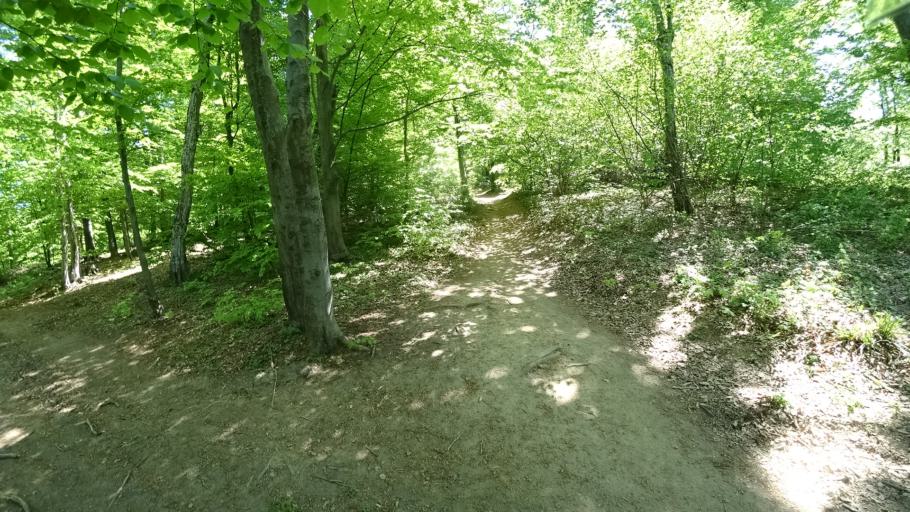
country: HR
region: Zagrebacka
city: Jablanovec
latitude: 45.8670
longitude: 15.8663
